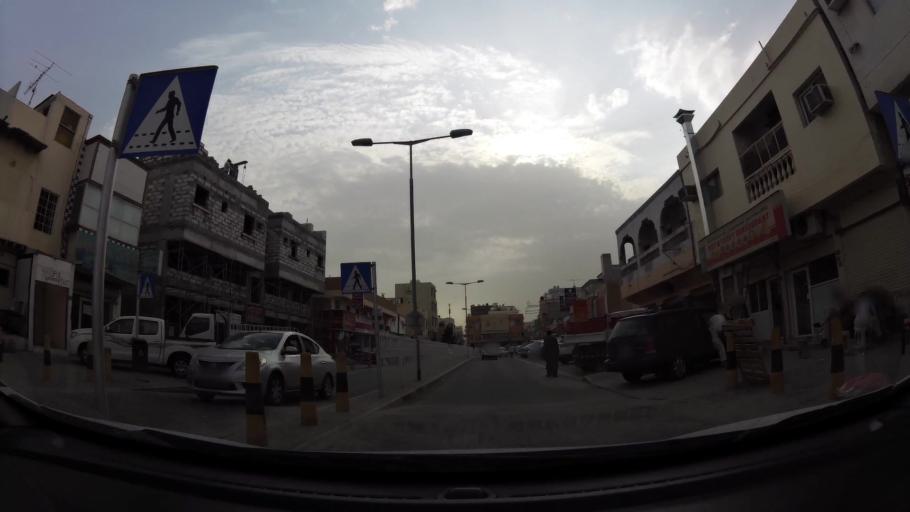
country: BH
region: Northern
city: Ar Rifa'
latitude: 26.1205
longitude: 50.5697
